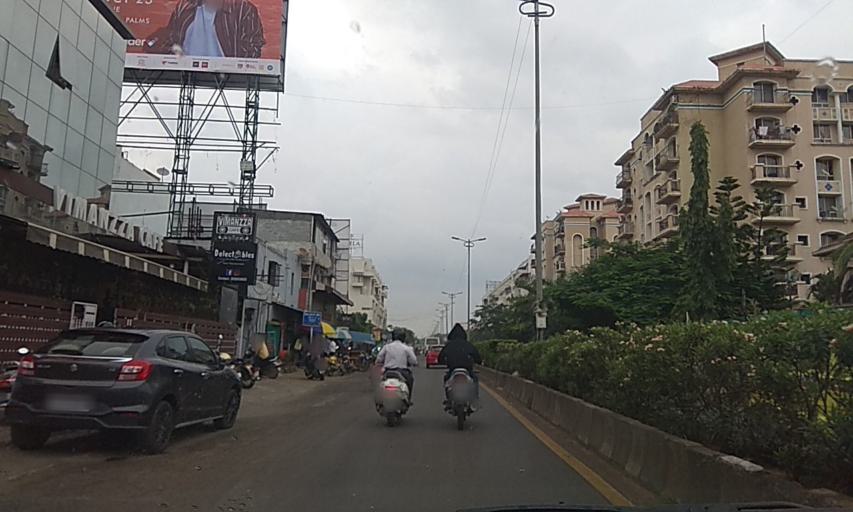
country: IN
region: Maharashtra
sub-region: Pune Division
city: Lohogaon
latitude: 18.5707
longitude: 73.9071
